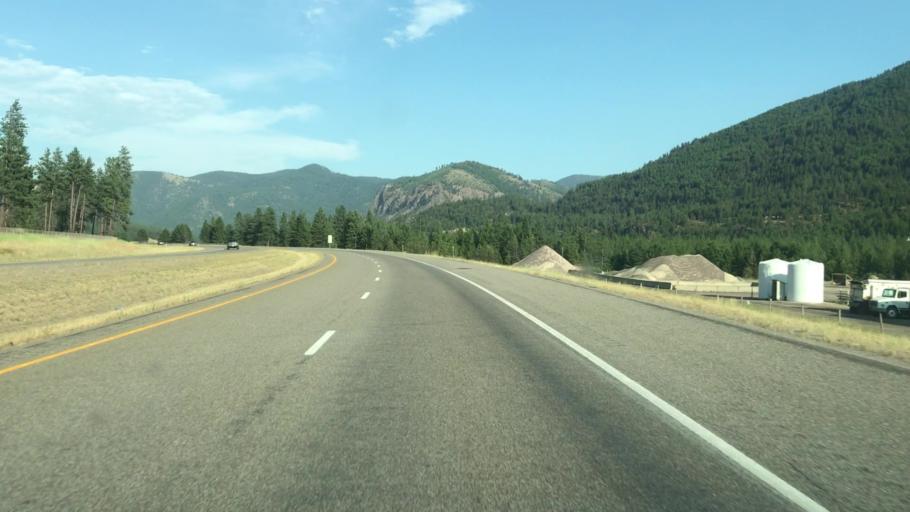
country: US
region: Montana
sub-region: Missoula County
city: Frenchtown
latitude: 47.0017
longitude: -114.4863
